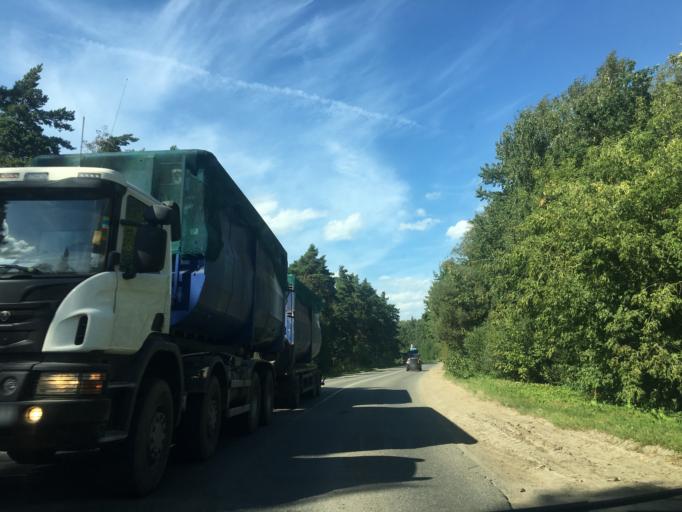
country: RU
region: Moskovskaya
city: Vidnoye
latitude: 55.5193
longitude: 37.6812
